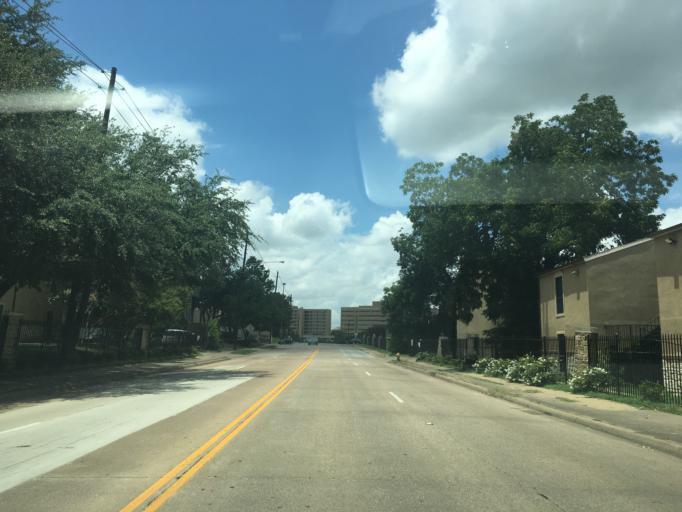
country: US
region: Texas
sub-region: Dallas County
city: University Park
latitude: 32.8777
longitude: -96.7570
